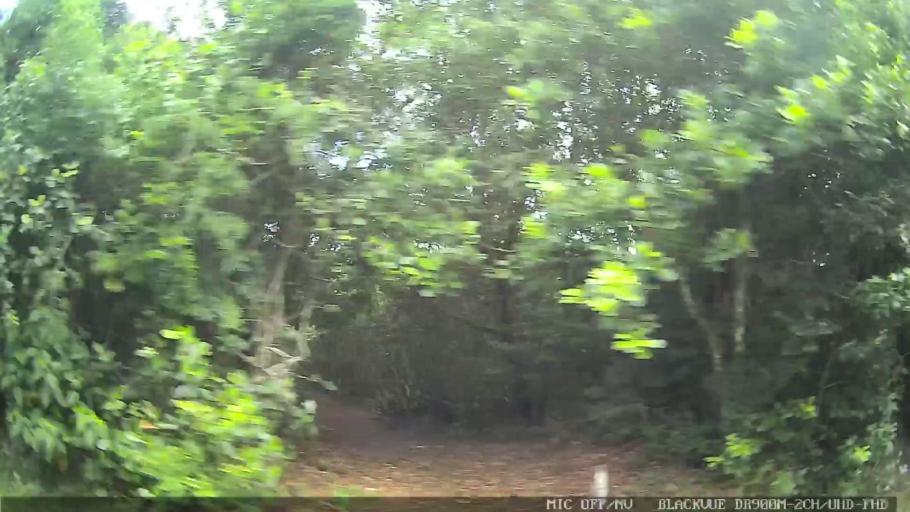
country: BR
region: Sao Paulo
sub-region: Iguape
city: Iguape
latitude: -24.6847
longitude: -47.4706
